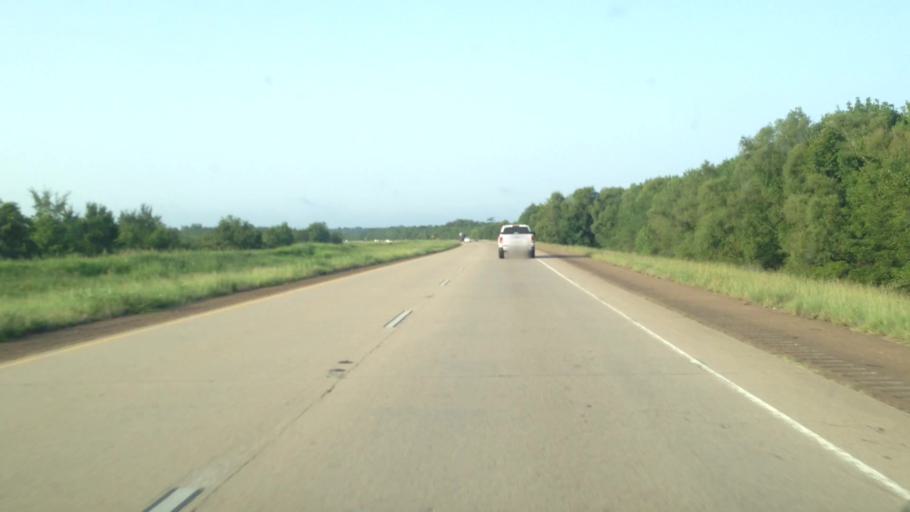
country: US
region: Louisiana
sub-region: Rapides Parish
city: Woodworth
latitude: 31.2076
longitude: -92.4726
